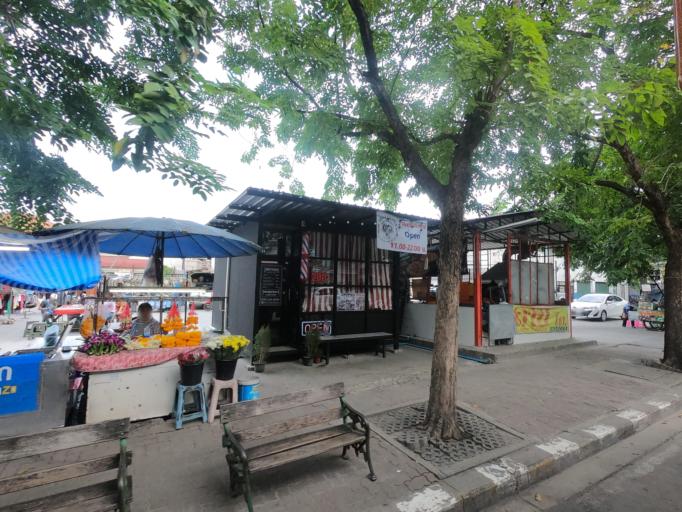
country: TH
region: Bangkok
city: Lat Phrao
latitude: 13.8198
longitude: 100.6095
